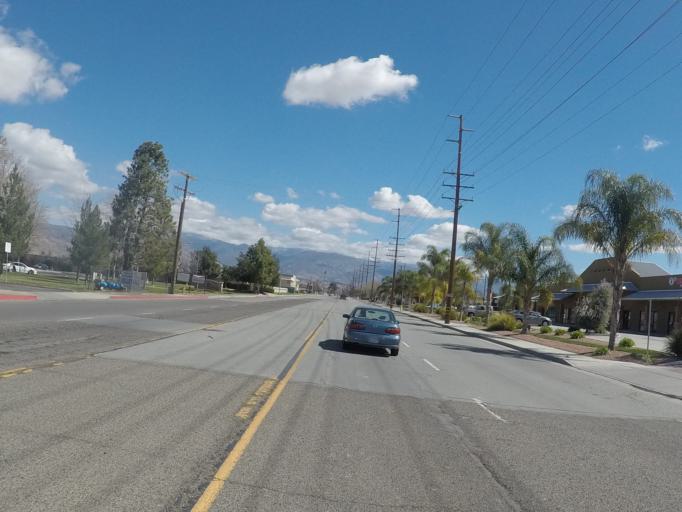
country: US
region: California
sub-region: Riverside County
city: San Jacinto
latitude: 33.7729
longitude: -116.9768
